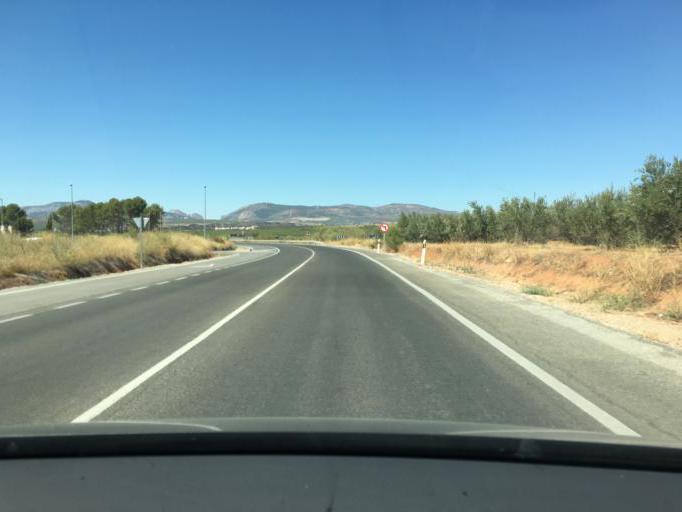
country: ES
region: Andalusia
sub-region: Provincia de Granada
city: Albolote
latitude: 37.2663
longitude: -3.6632
